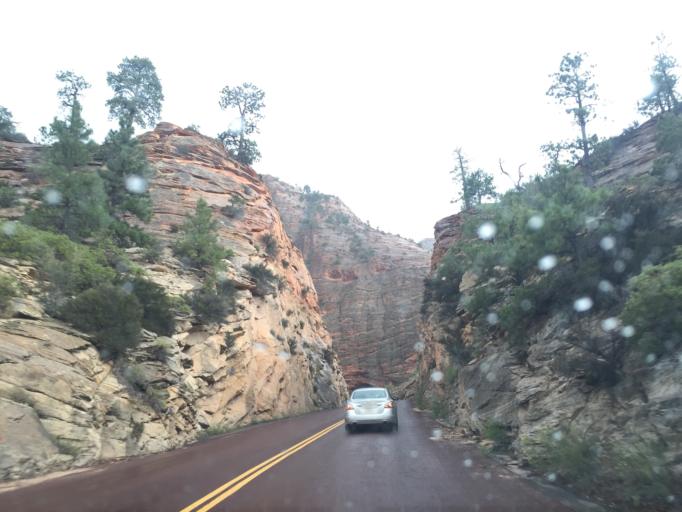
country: US
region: Utah
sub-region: Washington County
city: Hildale
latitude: 37.2150
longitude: -112.9349
